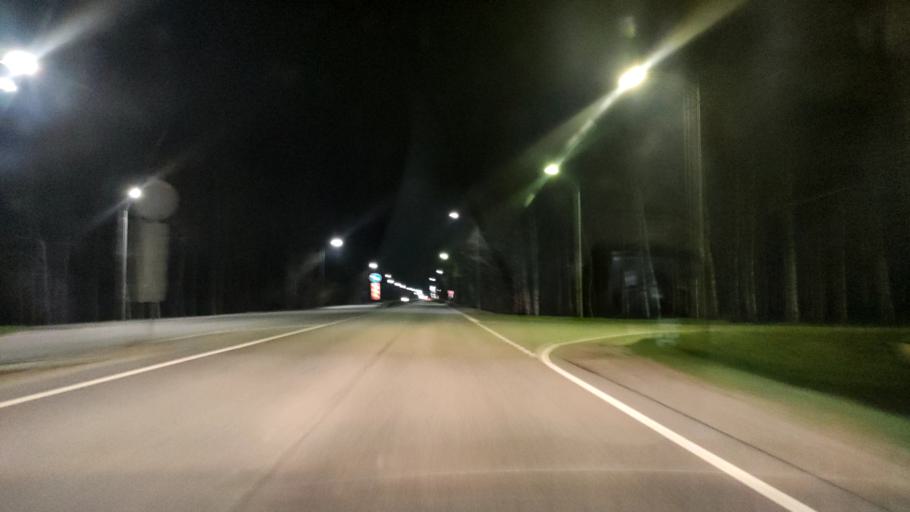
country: RU
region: Belgorod
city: Staryy Oskol
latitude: 51.4095
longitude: 37.8827
